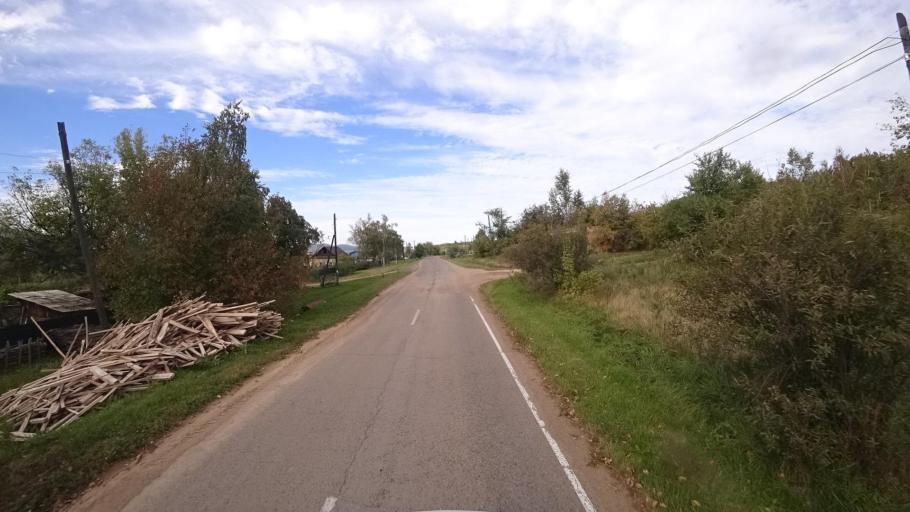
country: RU
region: Primorskiy
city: Dostoyevka
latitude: 44.3259
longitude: 133.4769
